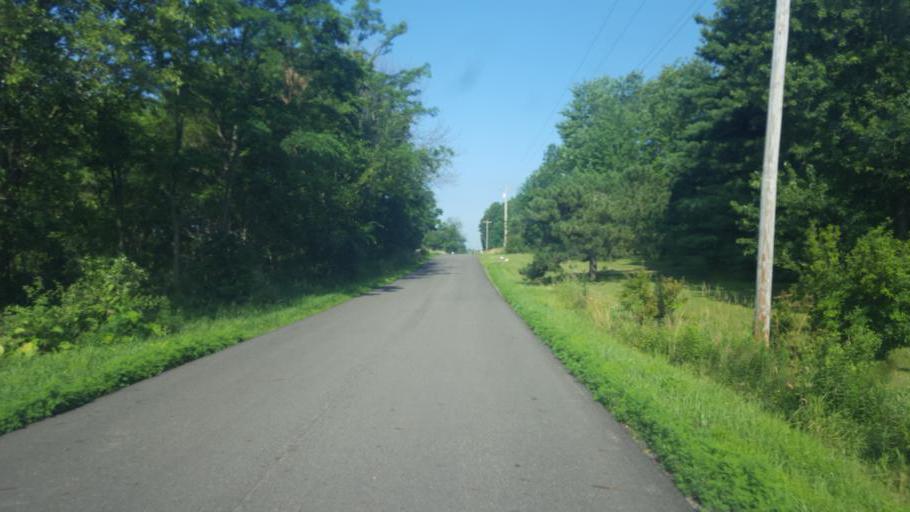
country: US
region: Ohio
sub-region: Crawford County
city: Galion
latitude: 40.6241
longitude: -82.7222
